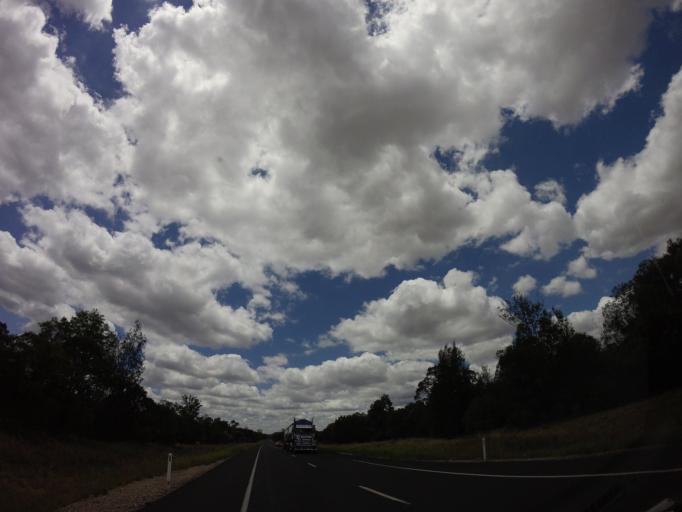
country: AU
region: Queensland
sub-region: Goondiwindi
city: Goondiwindi
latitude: -28.0542
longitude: 150.7754
